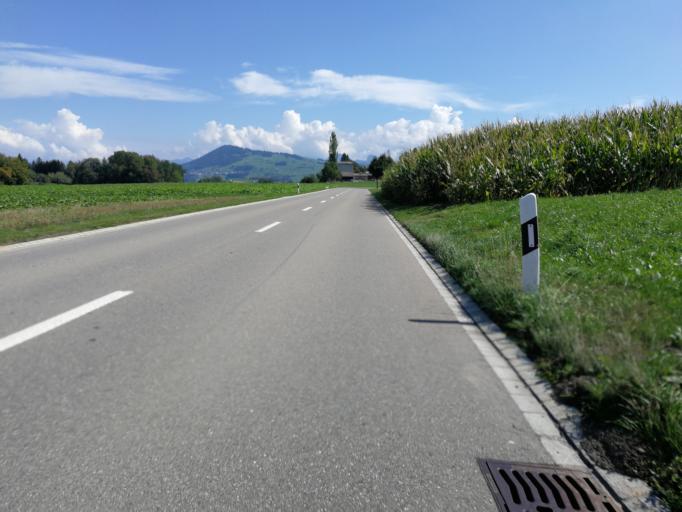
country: CH
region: Zurich
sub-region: Bezirk Horgen
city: Waedenswil / Eichweid
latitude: 47.2048
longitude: 8.6668
